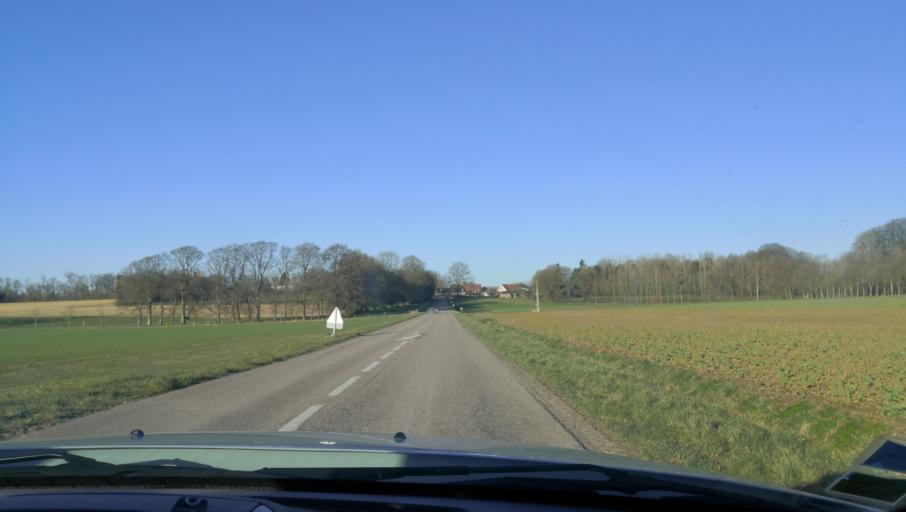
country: FR
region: Haute-Normandie
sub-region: Departement de la Seine-Maritime
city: Totes
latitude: 49.6592
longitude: 1.0227
